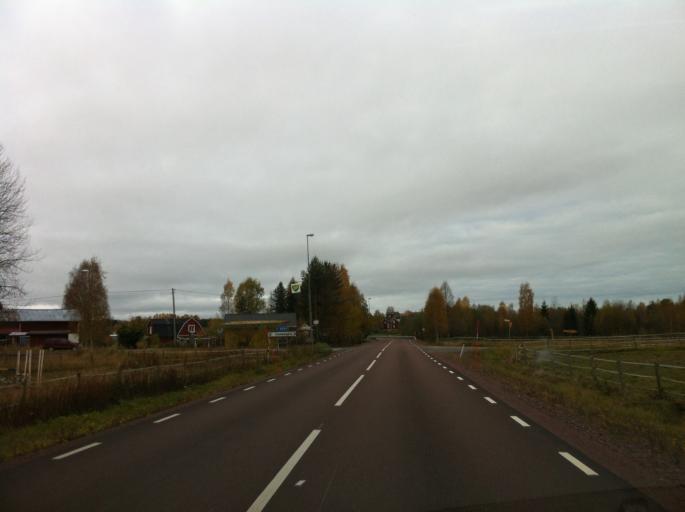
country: SE
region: Dalarna
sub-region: Orsa Kommun
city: Orsa
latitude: 61.1237
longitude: 14.4936
